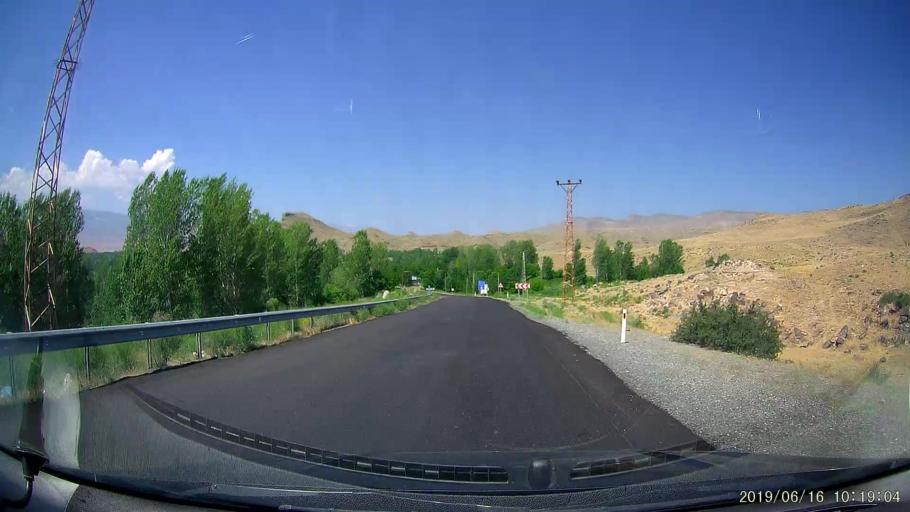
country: TR
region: Igdir
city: Tuzluca
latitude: 40.1561
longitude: 43.6603
